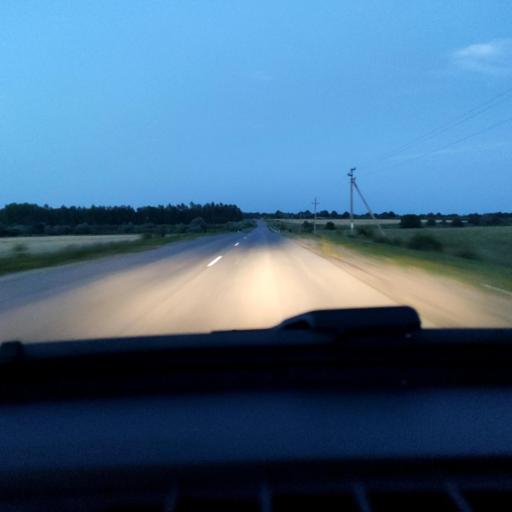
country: RU
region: Lipetsk
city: Zadonsk
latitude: 52.2967
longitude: 38.8311
